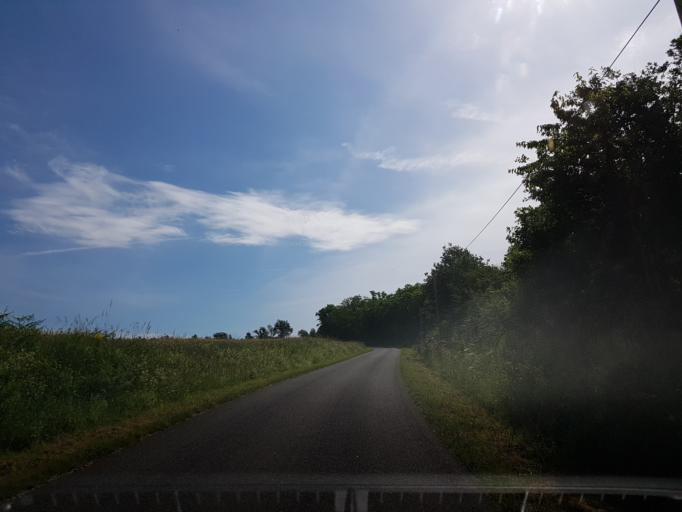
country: FR
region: Poitou-Charentes
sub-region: Departement de la Charente
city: Exideuil
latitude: 45.9149
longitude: 0.6642
